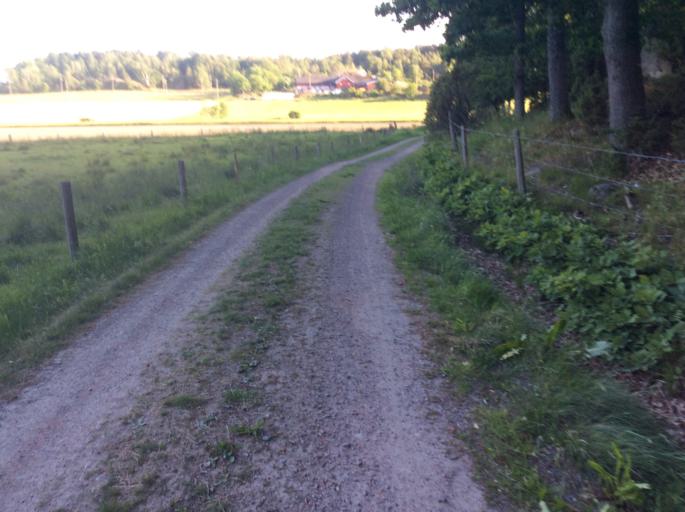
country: SE
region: Vaestra Goetaland
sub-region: Goteborg
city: Torslanda
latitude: 57.7939
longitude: 11.8574
